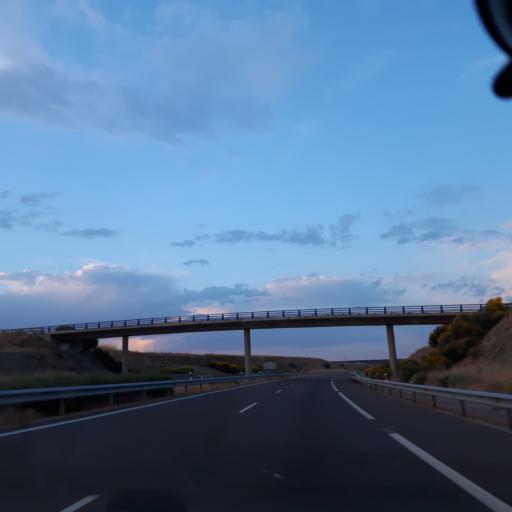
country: ES
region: Castille and Leon
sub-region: Provincia de Salamanca
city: Mozarbez
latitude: 40.8611
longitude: -5.6434
